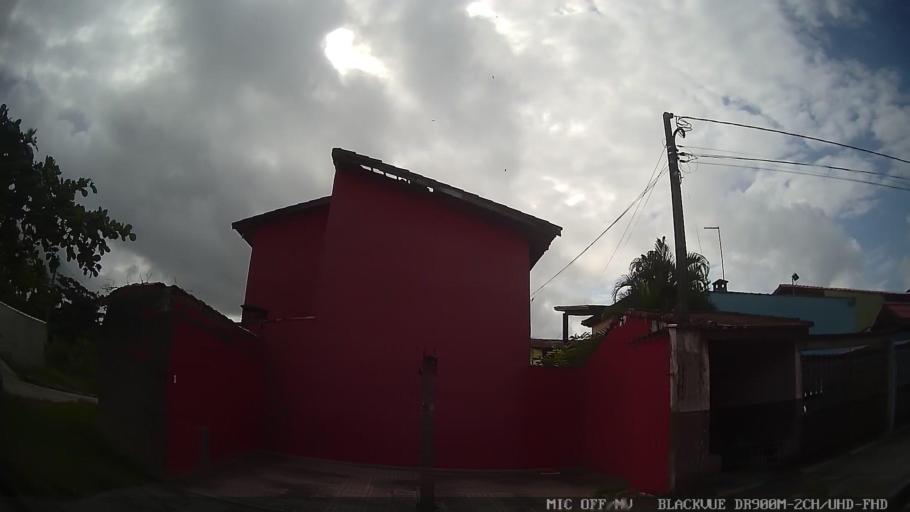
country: BR
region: Sao Paulo
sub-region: Itanhaem
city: Itanhaem
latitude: -24.1962
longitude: -46.8247
